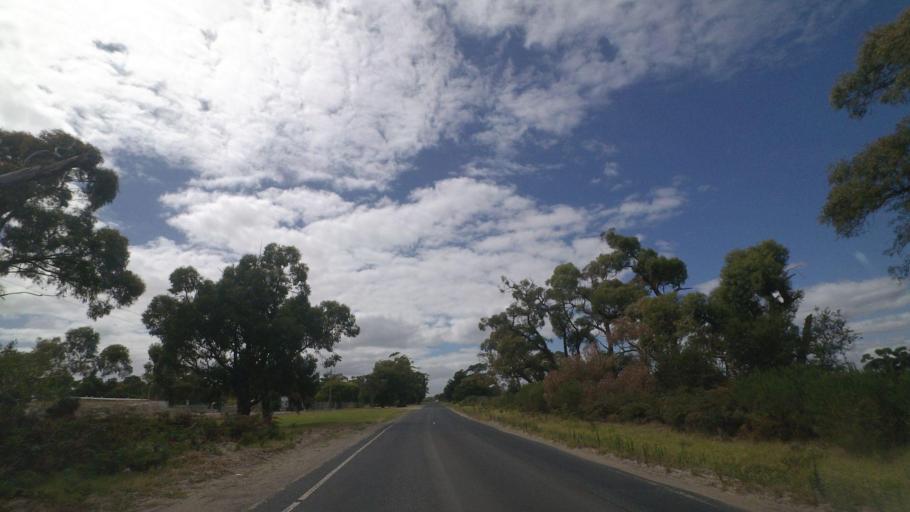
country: AU
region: Victoria
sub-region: Cardinia
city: Koo-Wee-Rup
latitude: -38.2776
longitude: 145.5801
